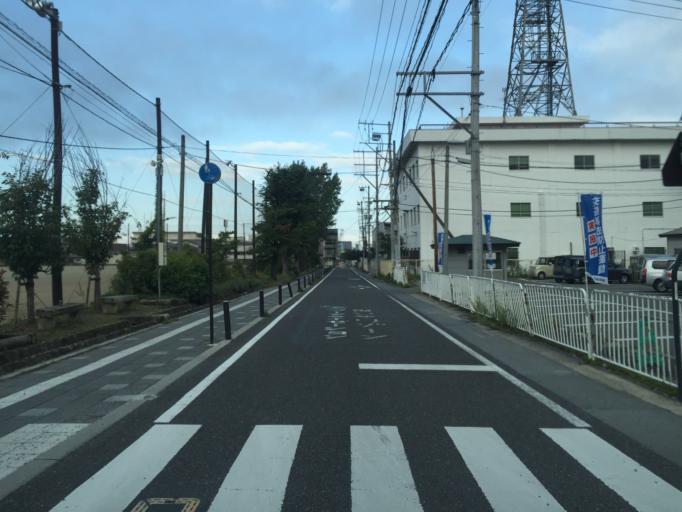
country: JP
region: Fukushima
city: Kitakata
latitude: 37.4939
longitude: 139.9298
